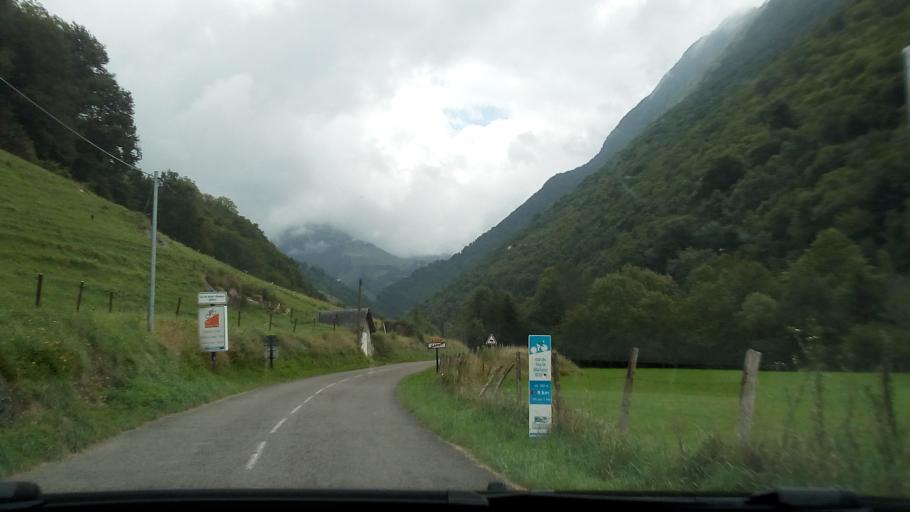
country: FR
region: Aquitaine
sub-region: Departement des Pyrenees-Atlantiques
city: Arette
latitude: 43.0768
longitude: -0.6056
